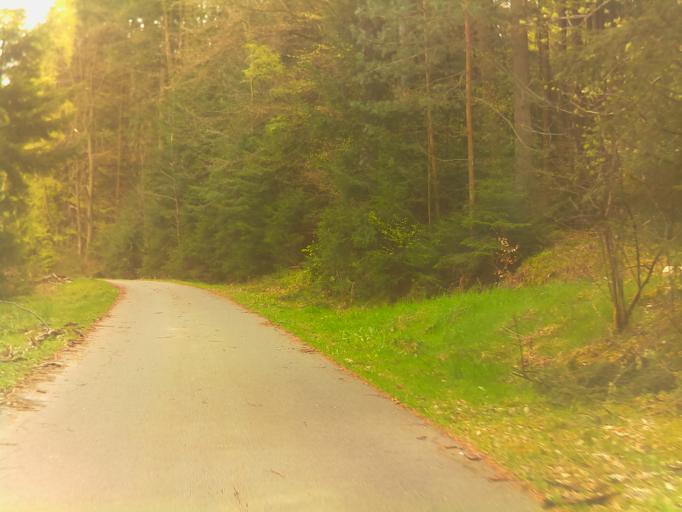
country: DE
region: Hesse
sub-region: Regierungsbezirk Darmstadt
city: Wald-Michelbach
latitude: 49.6347
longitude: 8.8968
